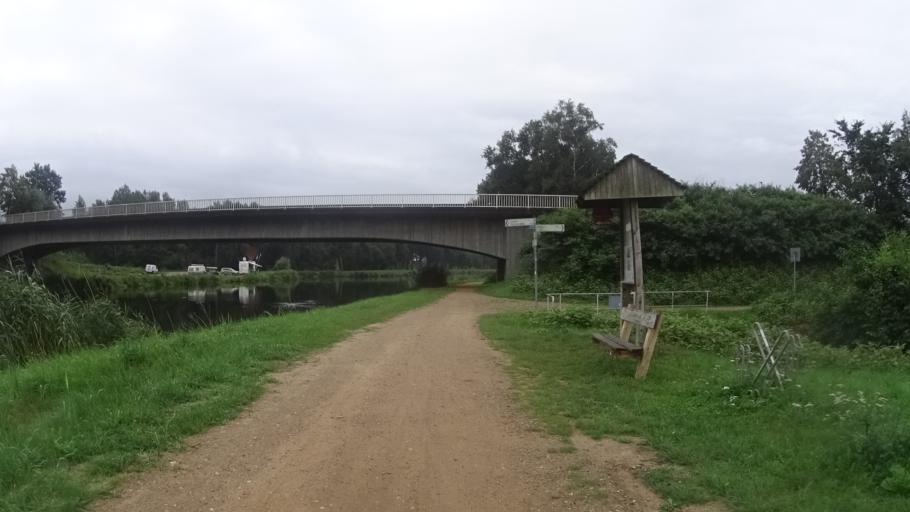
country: DE
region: Schleswig-Holstein
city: Buchen
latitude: 53.4800
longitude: 10.6311
